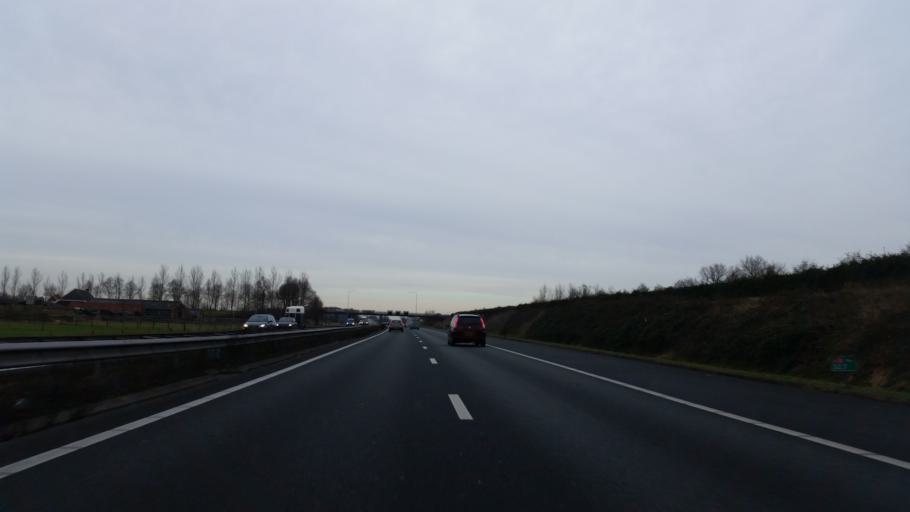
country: NL
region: Gelderland
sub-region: Gemeente Nijkerk
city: Nijkerk
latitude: 52.2189
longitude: 5.4511
